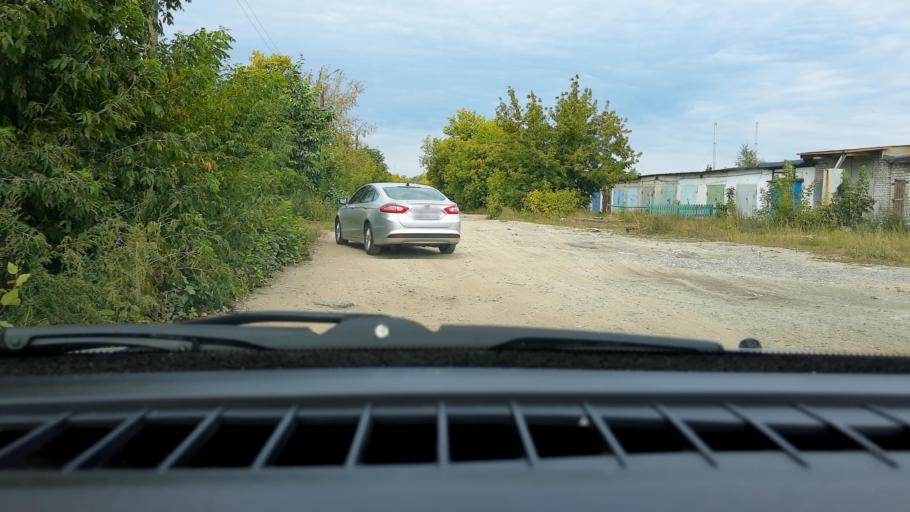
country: RU
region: Nizjnij Novgorod
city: Dzerzhinsk
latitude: 56.2468
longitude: 43.4811
